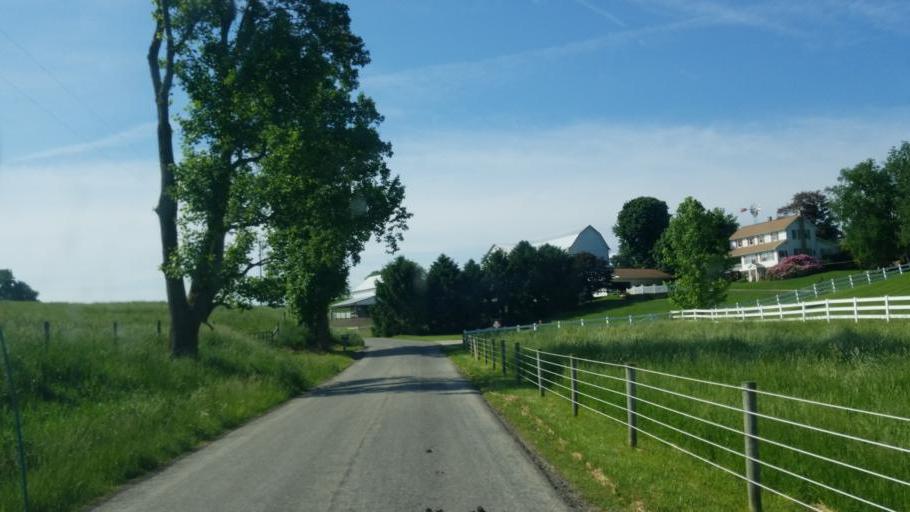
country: US
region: Ohio
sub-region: Tuscarawas County
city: Sugarcreek
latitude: 40.4940
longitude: -81.7721
